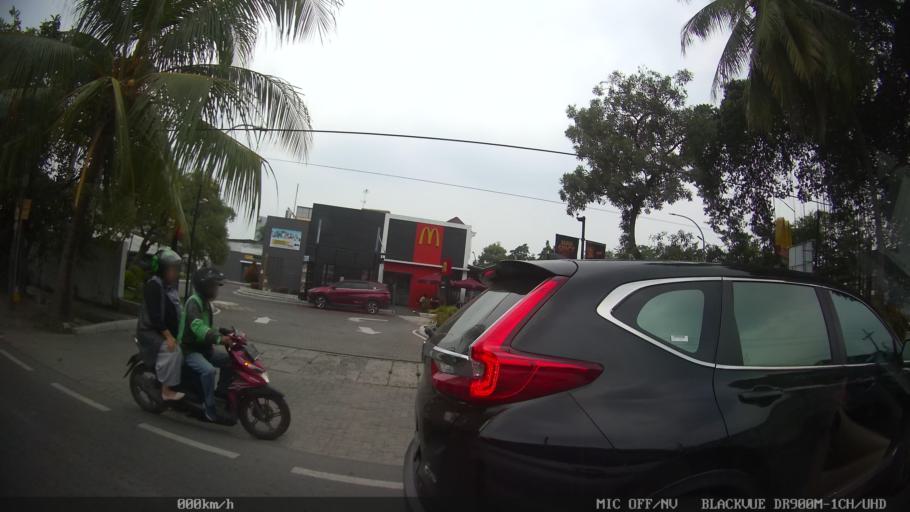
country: ID
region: North Sumatra
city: Medan
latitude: 3.5629
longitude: 98.6925
